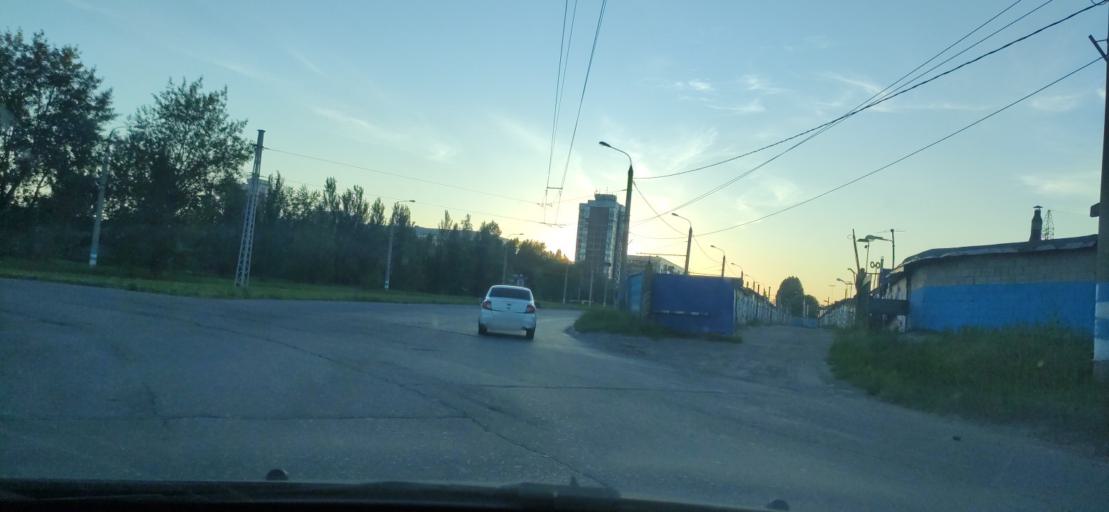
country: RU
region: Ulyanovsk
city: Mirnyy
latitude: 54.3802
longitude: 48.6236
